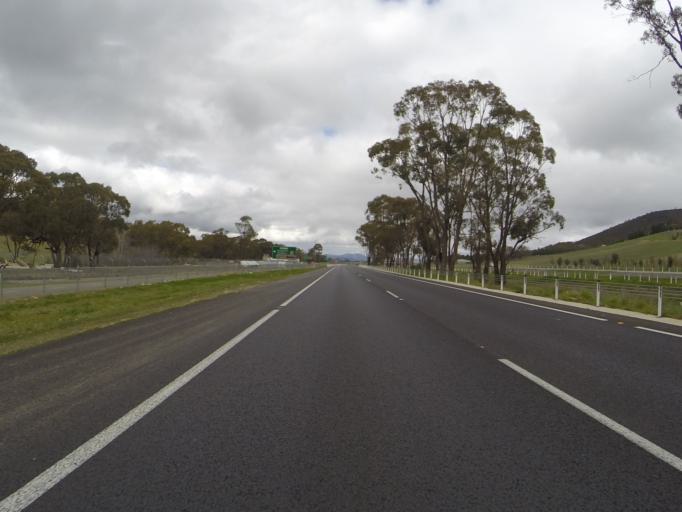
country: AU
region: Australian Capital Territory
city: Canberra
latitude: -35.2255
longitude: 149.1963
